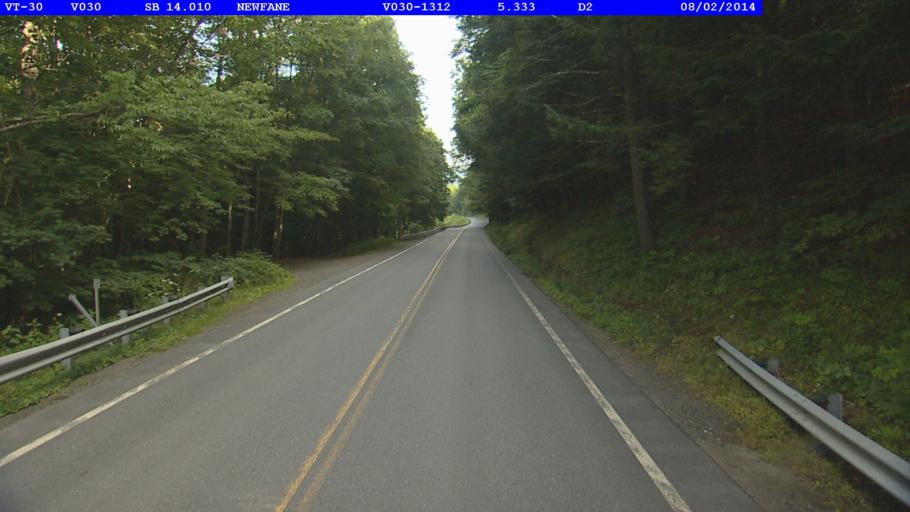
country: US
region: Vermont
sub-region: Windham County
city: Newfane
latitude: 43.0155
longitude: -72.6528
